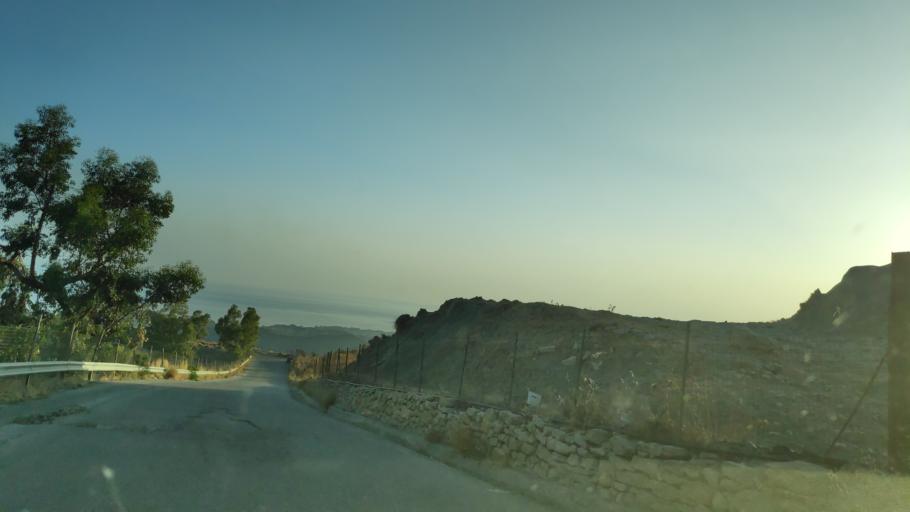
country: IT
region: Calabria
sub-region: Provincia di Reggio Calabria
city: Bova Marina
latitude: 37.9567
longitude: 15.9224
